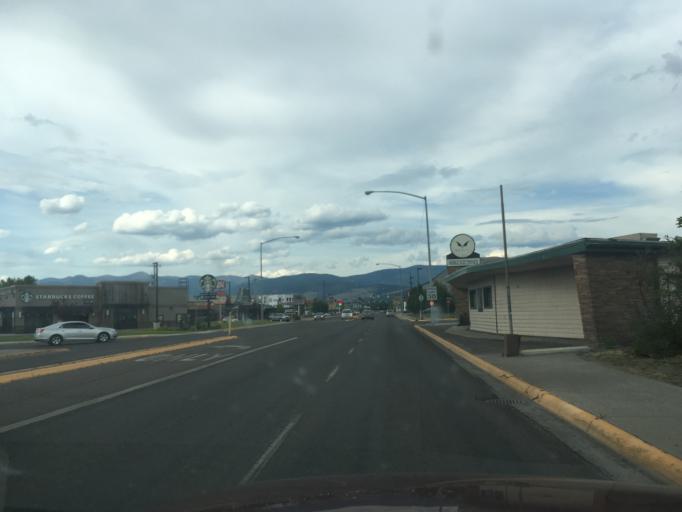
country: US
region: Montana
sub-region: Missoula County
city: Missoula
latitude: 46.8502
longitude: -114.0158
